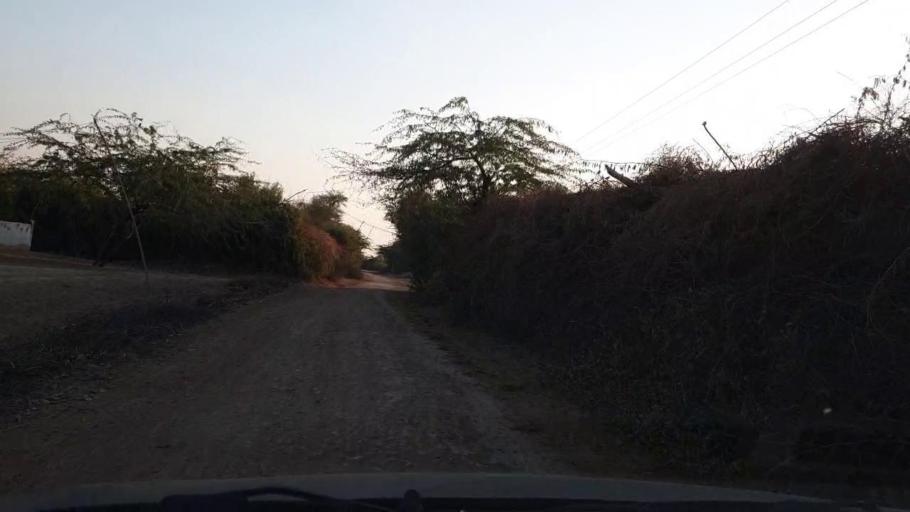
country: PK
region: Sindh
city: Jhol
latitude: 25.9185
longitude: 68.9338
